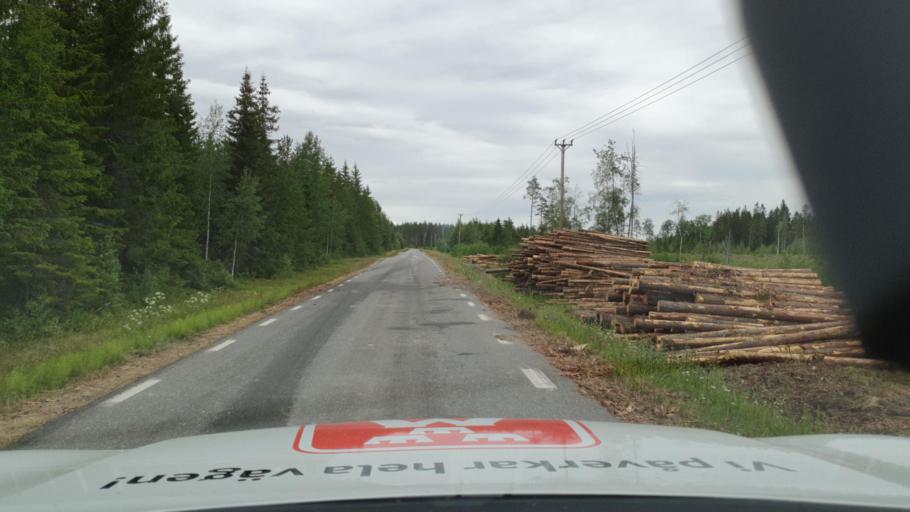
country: SE
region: Vaesterbotten
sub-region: Nordmalings Kommun
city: Nordmaling
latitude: 63.5132
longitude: 19.4213
